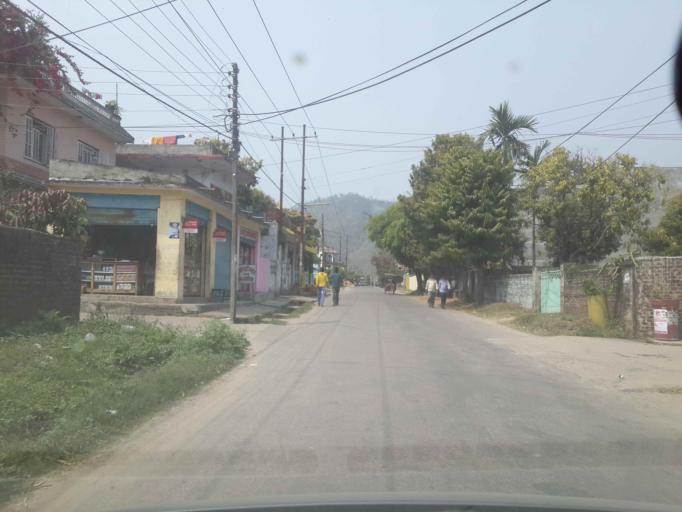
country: NP
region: Central Region
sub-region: Narayani Zone
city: Hitura
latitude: 27.4339
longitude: 85.0358
